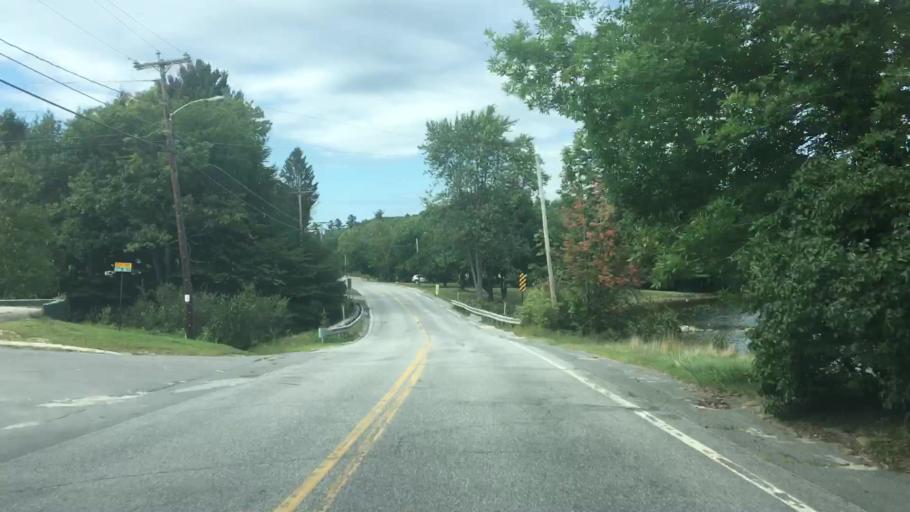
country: US
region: Maine
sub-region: Cumberland County
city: Raymond
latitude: 44.0091
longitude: -70.5230
